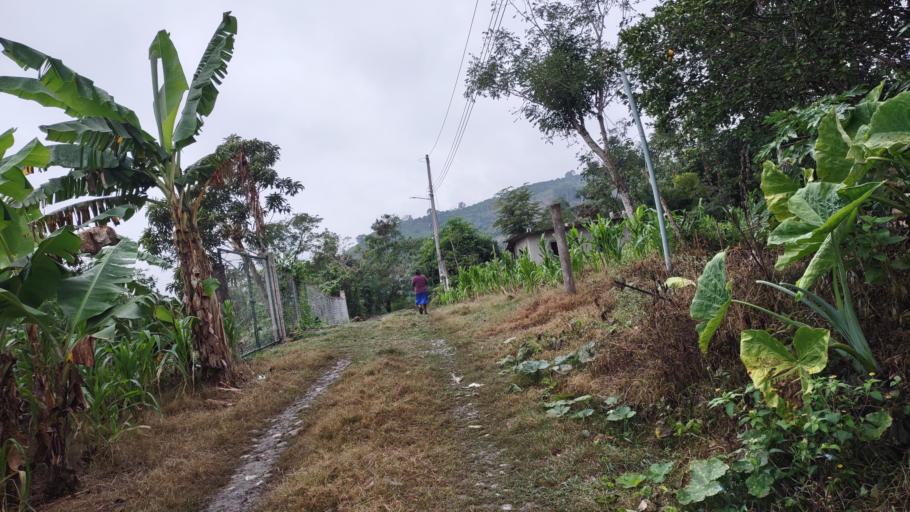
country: MX
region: Puebla
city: Espinal
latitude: 20.2638
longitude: -97.3679
